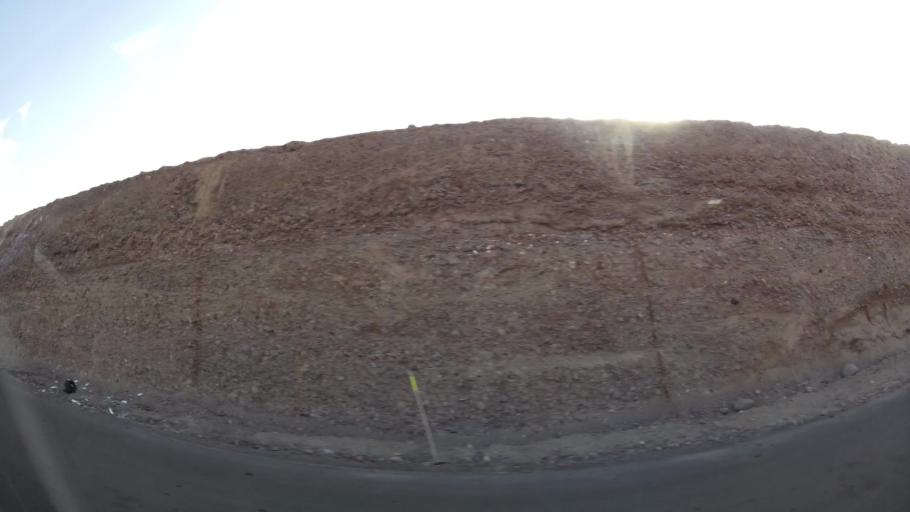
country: PE
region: Ica
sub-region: Provincia de Pisco
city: San Clemente
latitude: -13.6436
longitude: -76.1735
